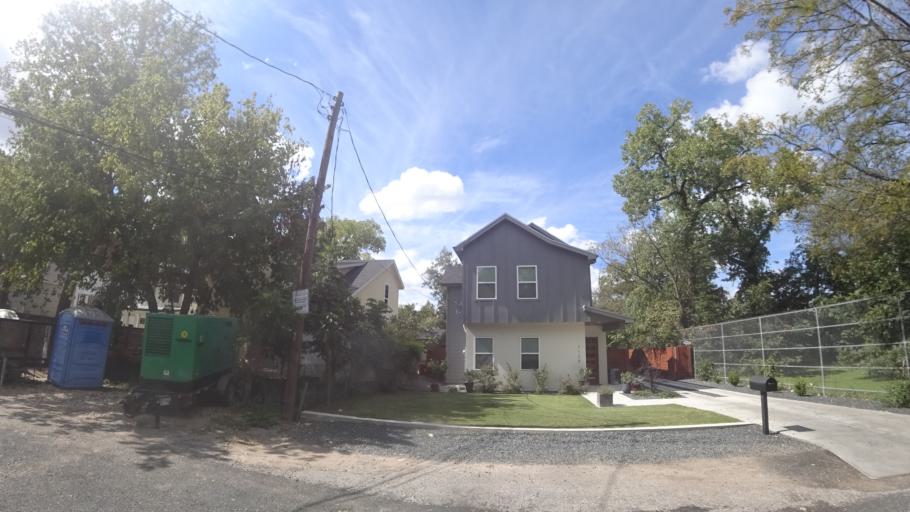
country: US
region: Texas
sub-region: Travis County
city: Austin
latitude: 30.2681
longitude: -97.7036
